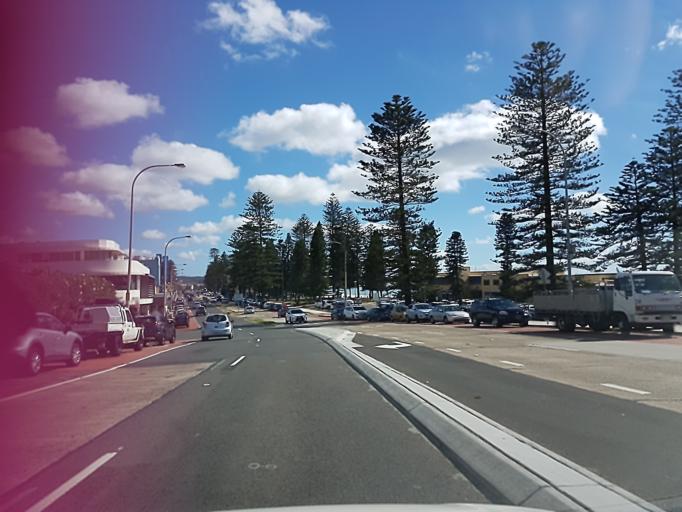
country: AU
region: New South Wales
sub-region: Warringah
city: Dee Why
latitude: -33.7341
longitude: 151.3021
